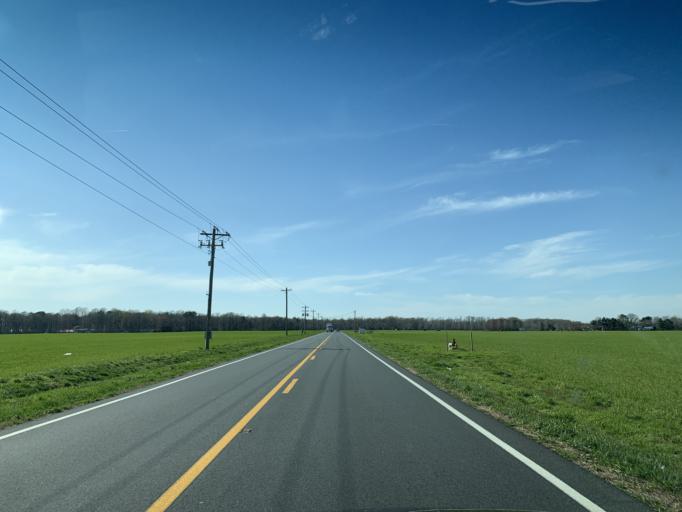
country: US
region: Delaware
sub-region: Sussex County
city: Milford
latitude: 38.9494
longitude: -75.4691
